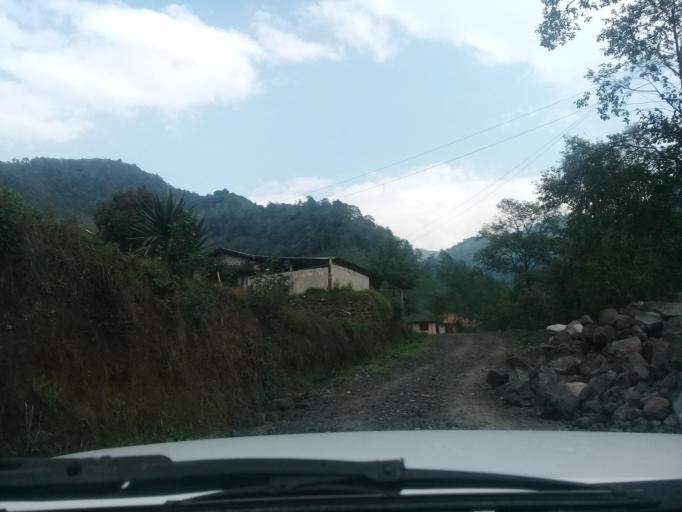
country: MX
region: Veracruz
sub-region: Mariano Escobedo
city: San Isidro el Berro
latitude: 18.9539
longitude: -97.1996
